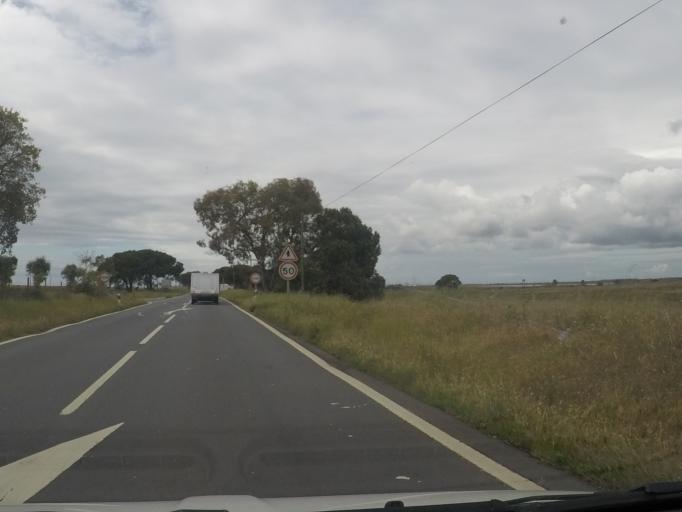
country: PT
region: Setubal
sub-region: Sines
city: Porto Covo
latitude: 37.8868
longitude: -8.7546
